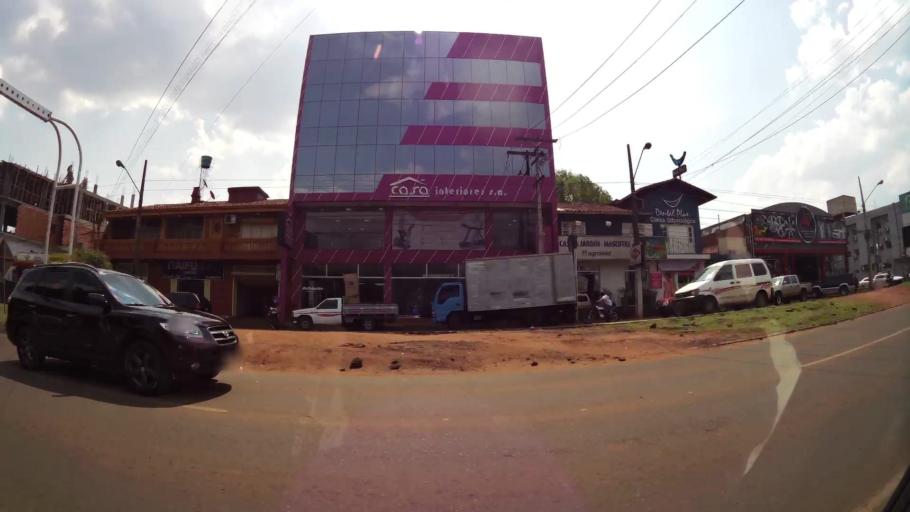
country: PY
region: Alto Parana
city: Ciudad del Este
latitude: -25.5123
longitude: -54.6407
